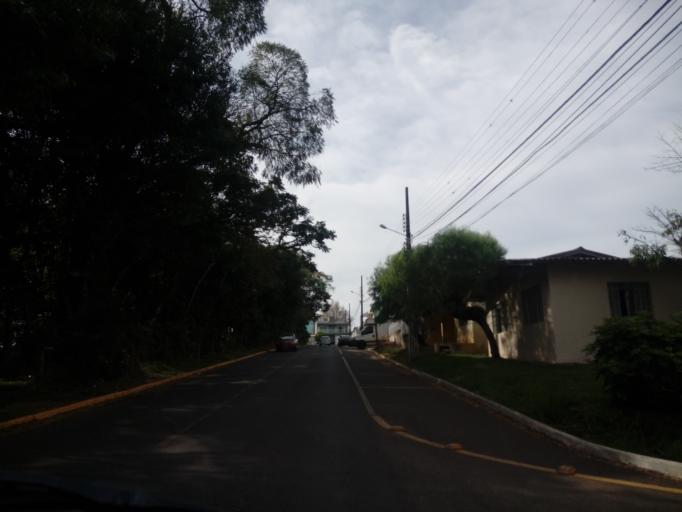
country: BR
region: Santa Catarina
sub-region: Chapeco
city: Chapeco
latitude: -27.1218
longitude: -52.6161
